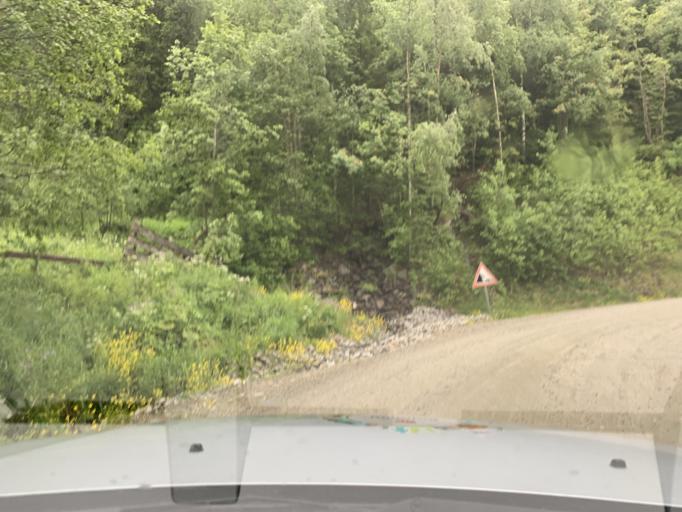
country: NO
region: Oppland
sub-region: Oyer
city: Tretten
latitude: 61.3935
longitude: 10.2738
